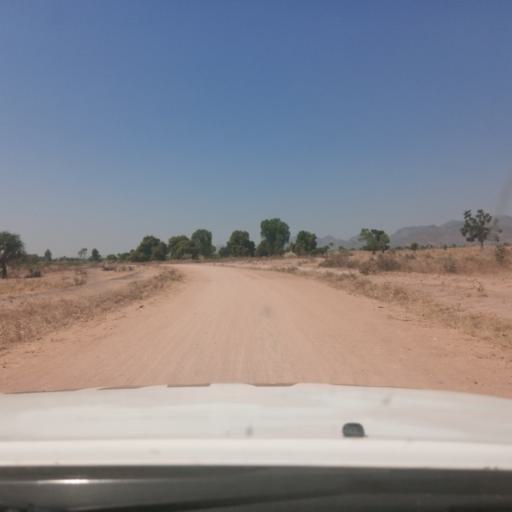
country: NG
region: Adamawa
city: Little Gombi
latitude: 9.7779
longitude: 12.5844
